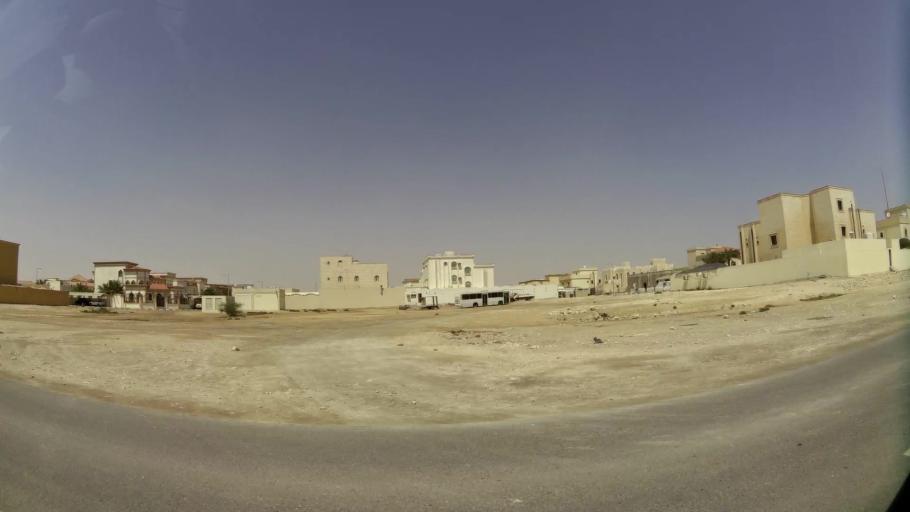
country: QA
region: Baladiyat Umm Salal
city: Umm Salal Muhammad
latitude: 25.4034
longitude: 51.4520
